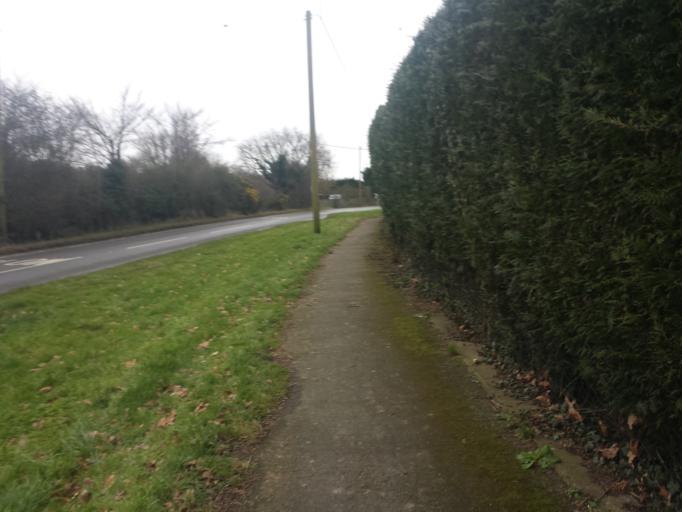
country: GB
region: England
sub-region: Essex
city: Little Clacton
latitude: 51.8994
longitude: 1.1849
